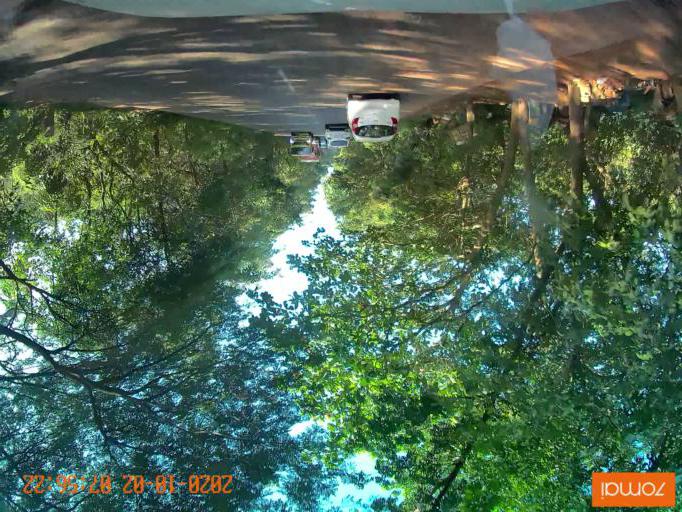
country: IN
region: Kerala
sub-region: Kozhikode
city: Ferokh
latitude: 11.1905
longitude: 75.8696
